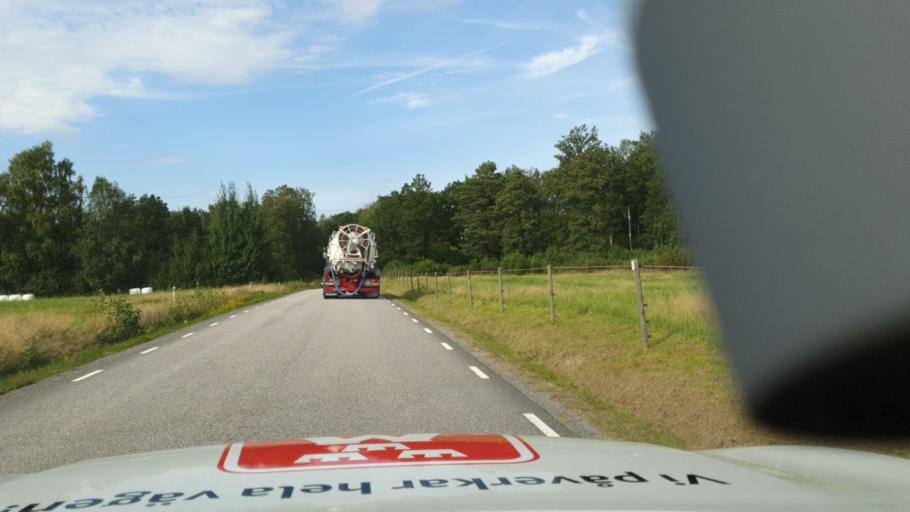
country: SE
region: Vaestra Goetaland
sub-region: Marks Kommun
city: Kinna
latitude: 57.4535
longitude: 12.7027
